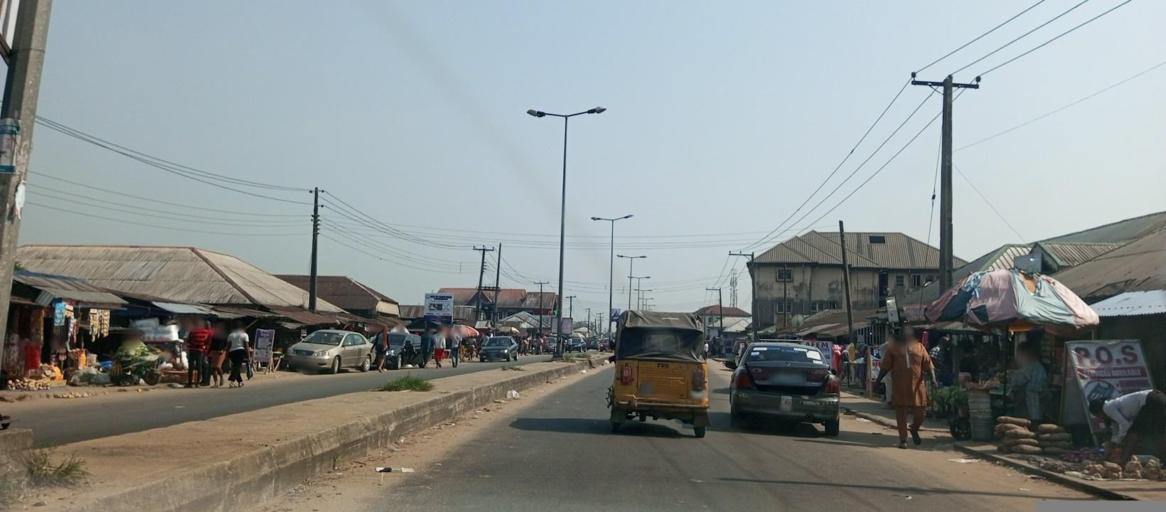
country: NG
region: Rivers
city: Emuoha
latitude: 4.8888
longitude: 6.9012
